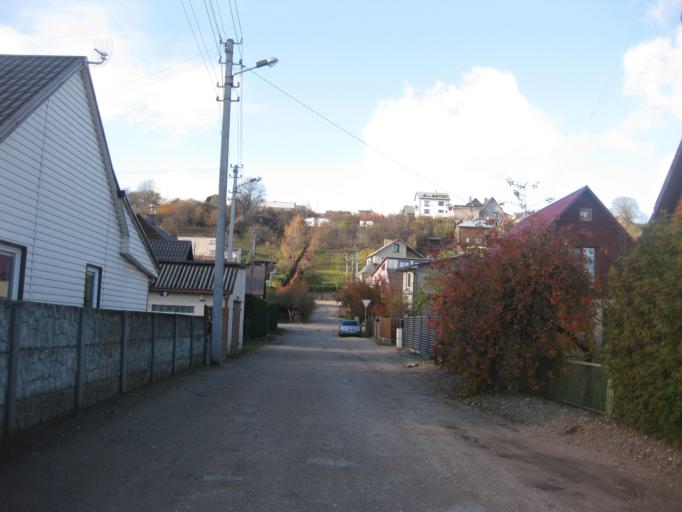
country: LT
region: Kauno apskritis
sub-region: Kaunas
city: Silainiai
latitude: 54.9212
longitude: 23.8988
